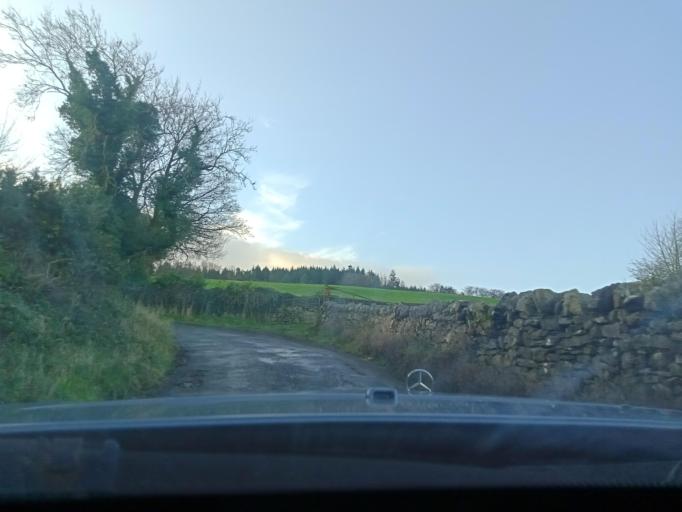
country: IE
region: Leinster
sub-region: Kilkenny
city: Callan
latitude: 52.4701
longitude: -7.4247
